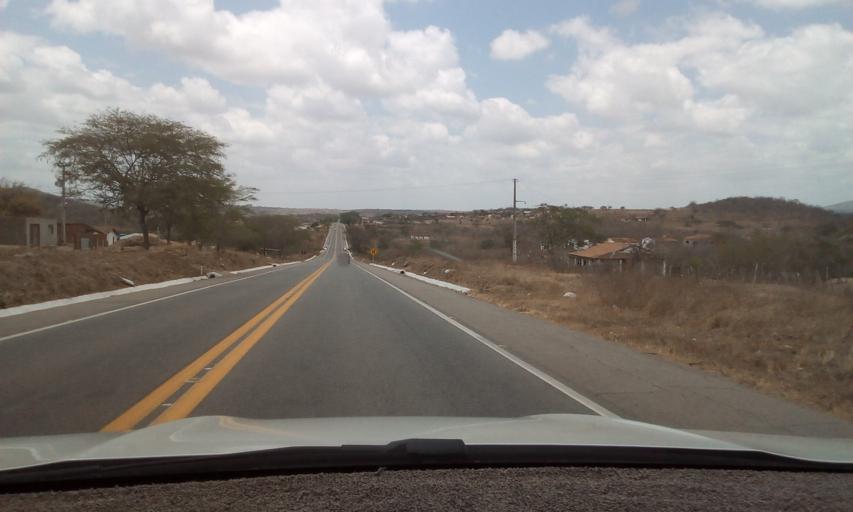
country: BR
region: Pernambuco
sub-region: Taquaritinga Do Norte
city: Taquaritinga do Norte
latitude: -7.6955
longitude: -36.0614
